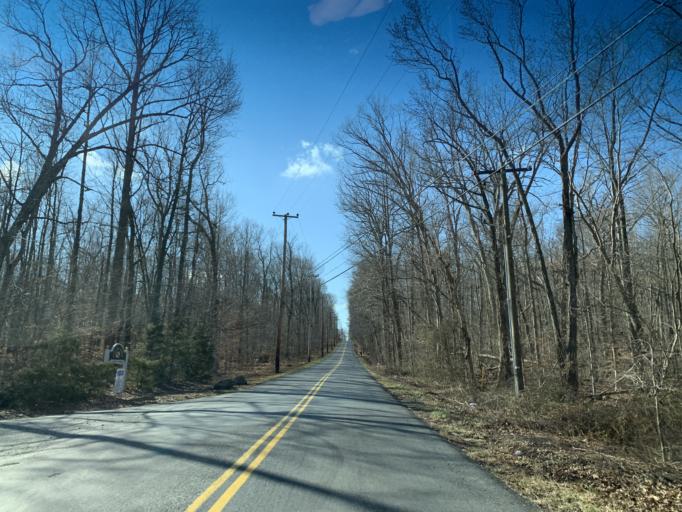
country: US
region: Maryland
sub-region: Harford County
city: Riverside
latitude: 39.5254
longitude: -76.2239
